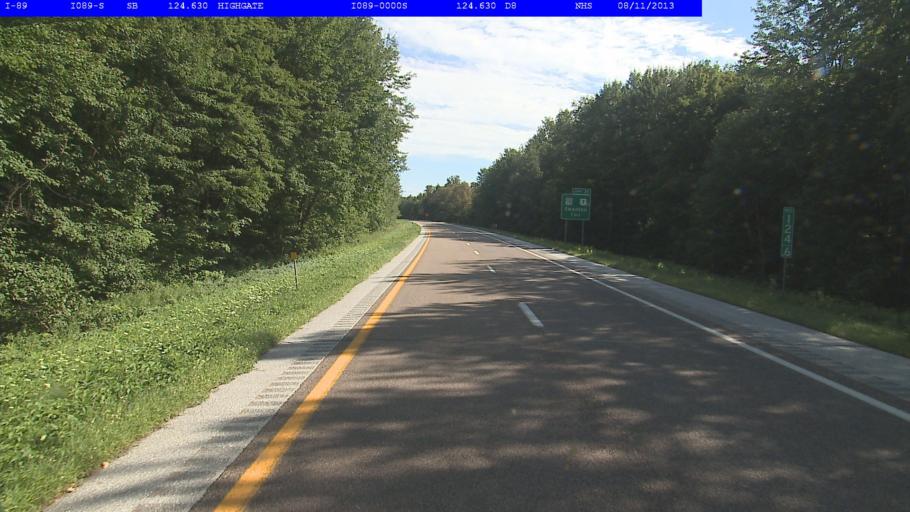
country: US
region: Vermont
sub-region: Franklin County
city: Swanton
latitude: 44.9396
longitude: -73.1154
